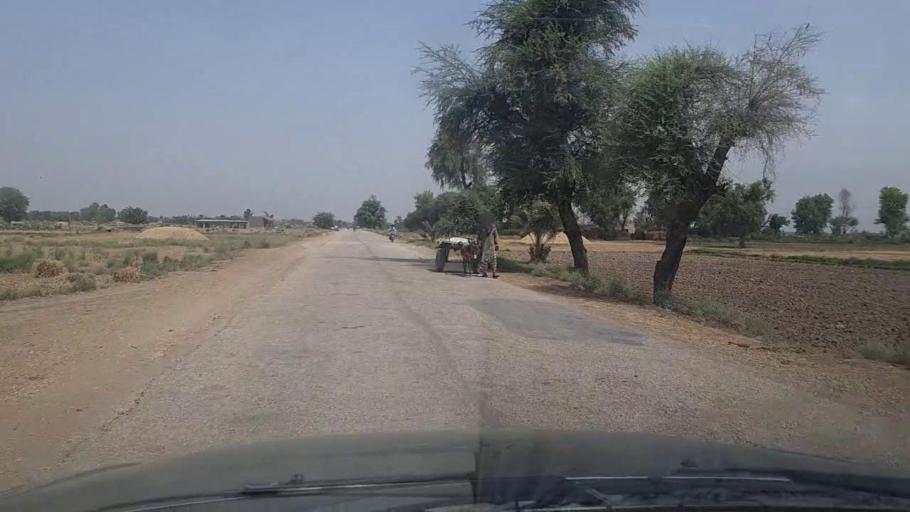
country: PK
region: Sindh
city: Setharja Old
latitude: 27.1547
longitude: 68.5215
